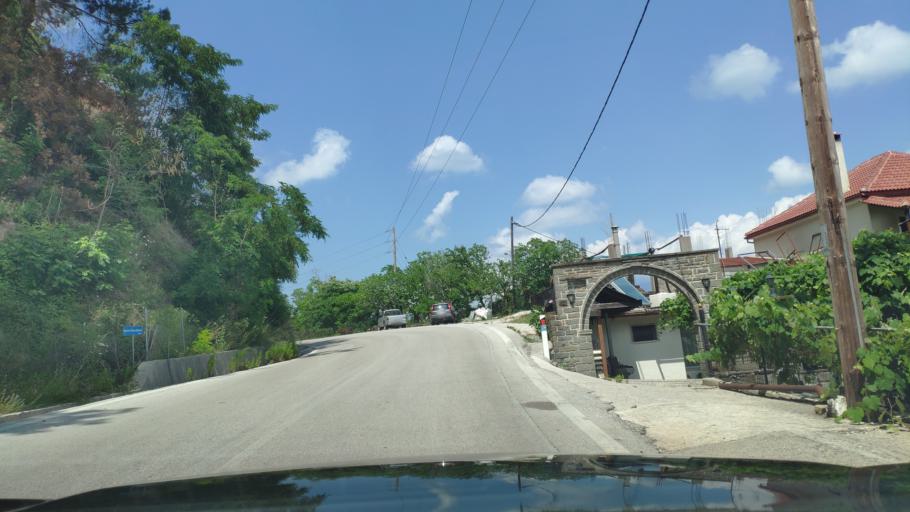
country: GR
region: Epirus
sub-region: Nomos Artas
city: Agios Dimitrios
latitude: 39.3230
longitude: 20.9948
